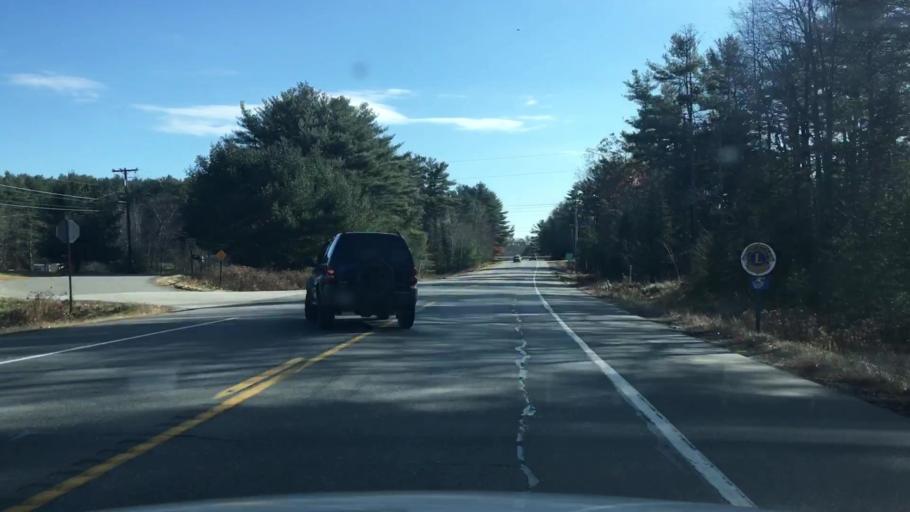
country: US
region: Maine
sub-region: Kennebec County
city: Windsor
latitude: 44.2638
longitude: -69.5603
